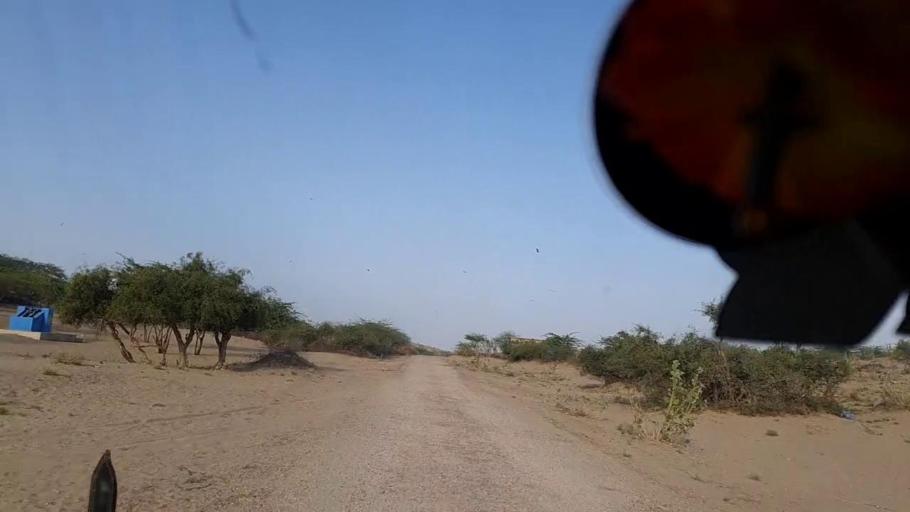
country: PK
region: Sindh
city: Diplo
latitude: 24.5653
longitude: 69.4873
